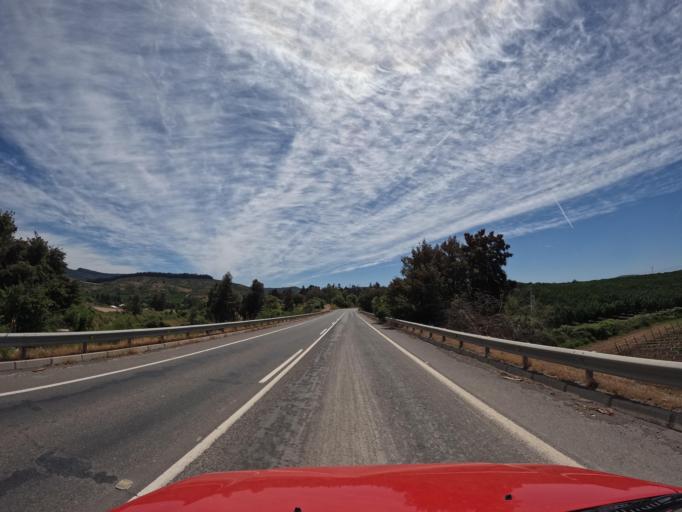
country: CL
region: Maule
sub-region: Provincia de Talca
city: Talca
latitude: -35.2940
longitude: -71.5298
